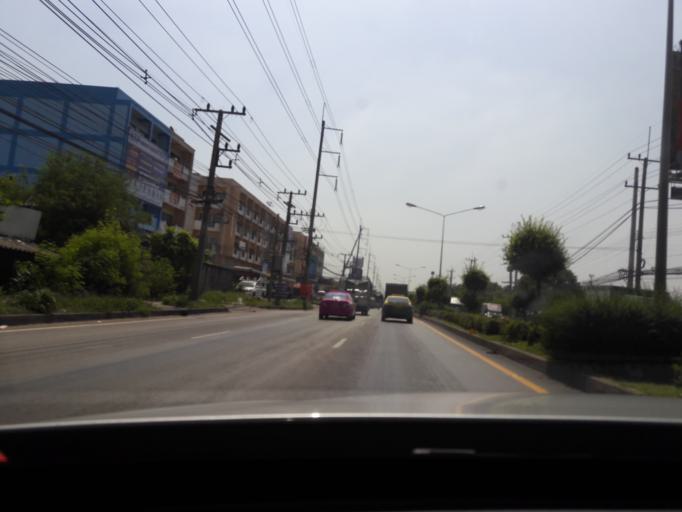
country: TH
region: Samut Sakhon
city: Samut Sakhon
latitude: 13.5902
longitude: 100.2805
